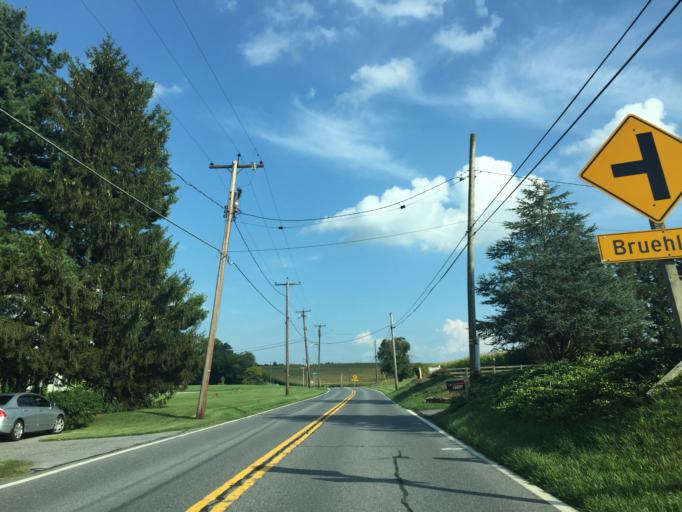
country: US
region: Maryland
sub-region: Carroll County
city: Hampstead
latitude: 39.5950
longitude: -76.7532
